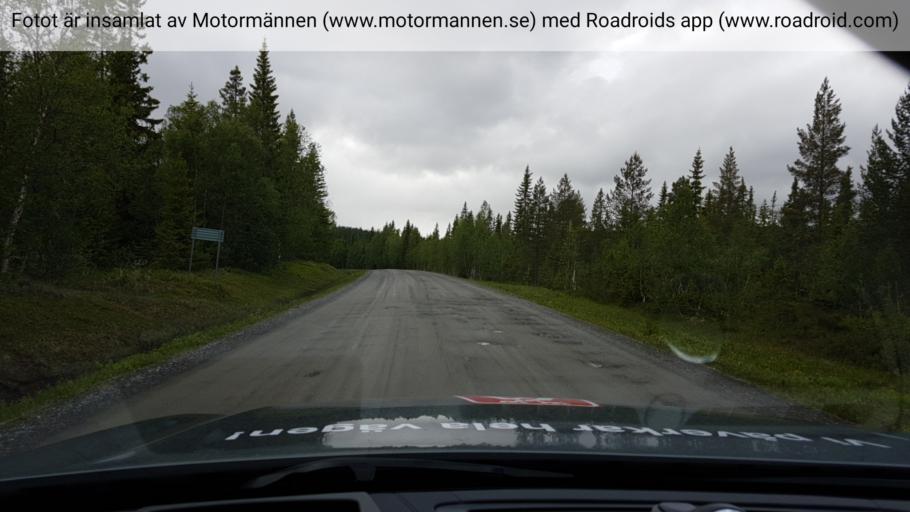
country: SE
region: Jaemtland
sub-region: Are Kommun
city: Are
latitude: 63.7140
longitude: 12.6253
